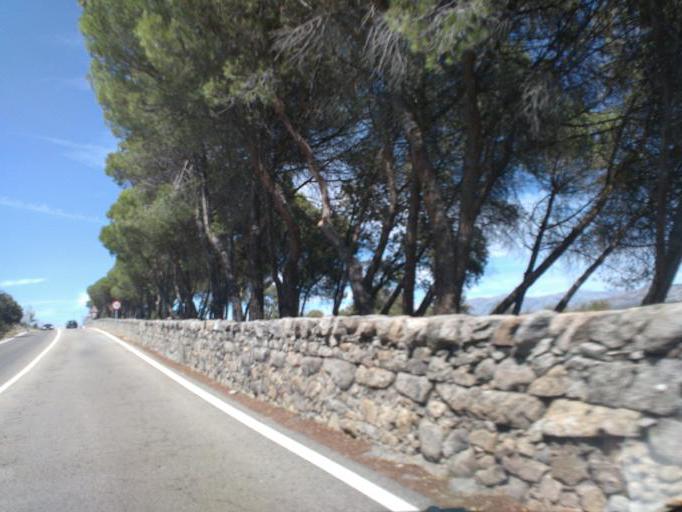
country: ES
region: Madrid
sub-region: Provincia de Madrid
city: Galapagar
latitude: 40.5660
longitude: -3.9746
